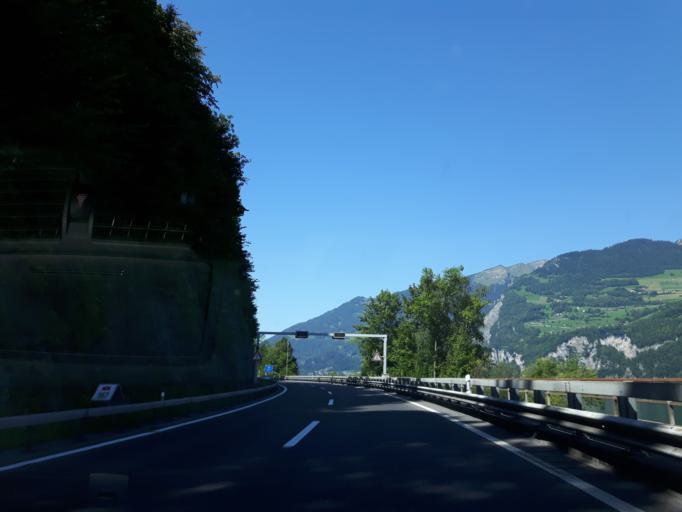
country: CH
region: Saint Gallen
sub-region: Wahlkreis See-Gaster
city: Amden
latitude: 47.1218
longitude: 9.1566
